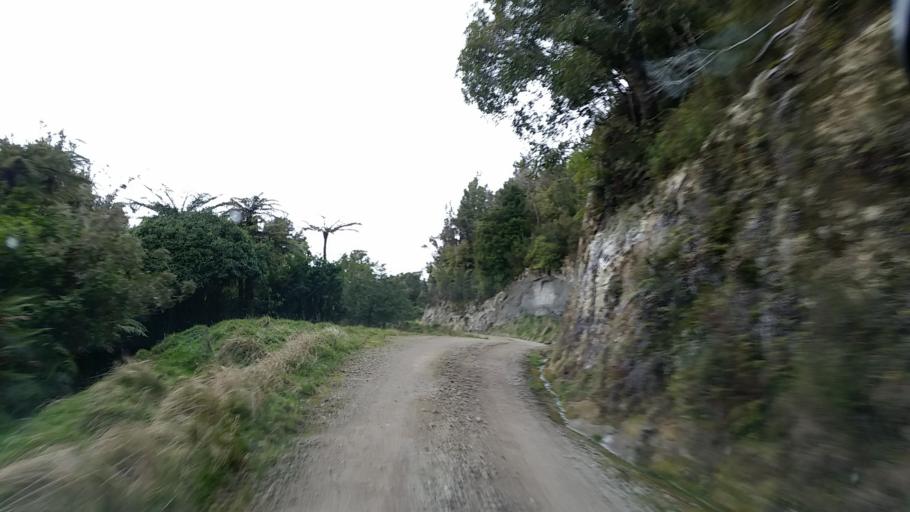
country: NZ
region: Taranaki
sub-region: South Taranaki District
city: Patea
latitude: -39.5802
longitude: 174.6923
